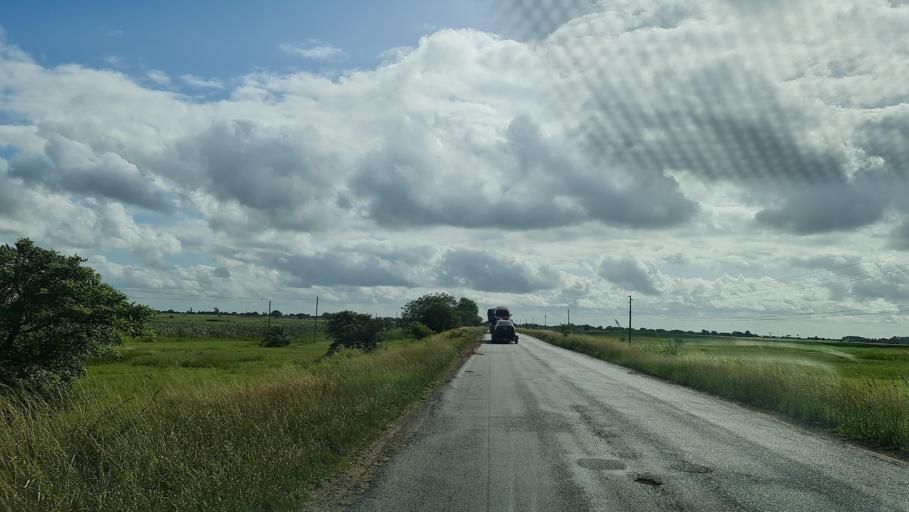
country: MZ
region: Gaza
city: Macia
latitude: -25.0970
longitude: 32.8292
